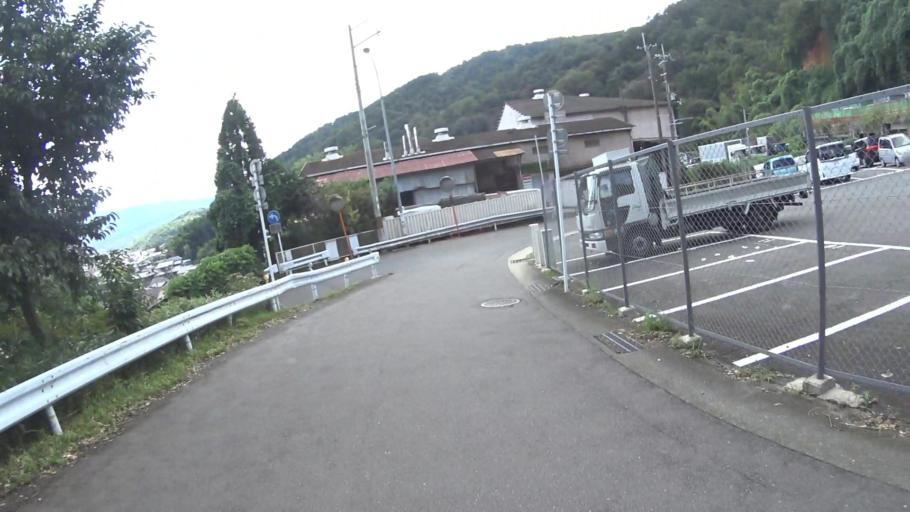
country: JP
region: Kyoto
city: Kyoto
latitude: 34.9753
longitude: 135.7912
